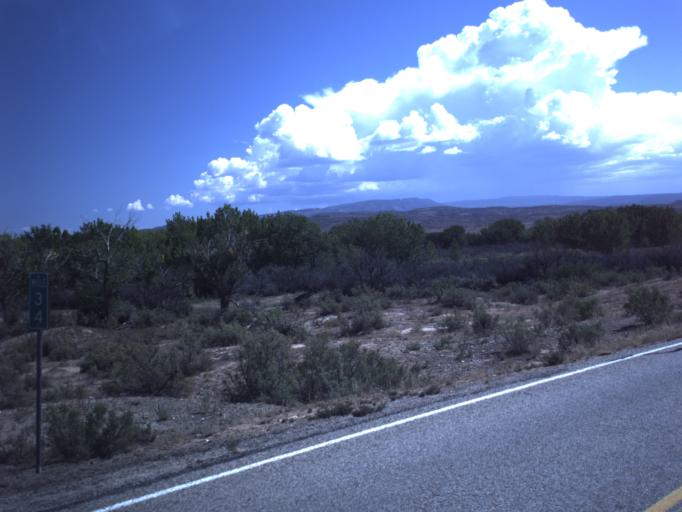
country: US
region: Utah
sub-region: Grand County
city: Moab
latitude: 38.8582
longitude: -109.2911
